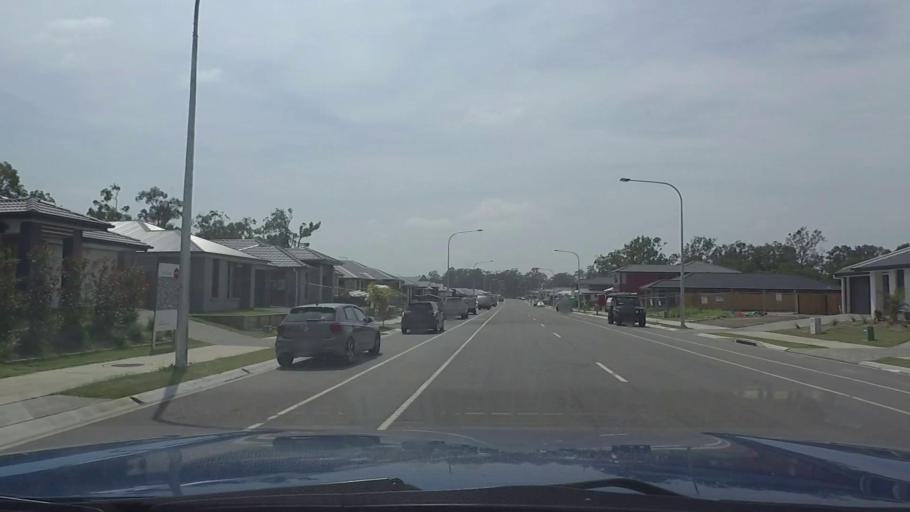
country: AU
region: Queensland
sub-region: Logan
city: Logan Reserve
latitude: -27.7042
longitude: 153.1017
